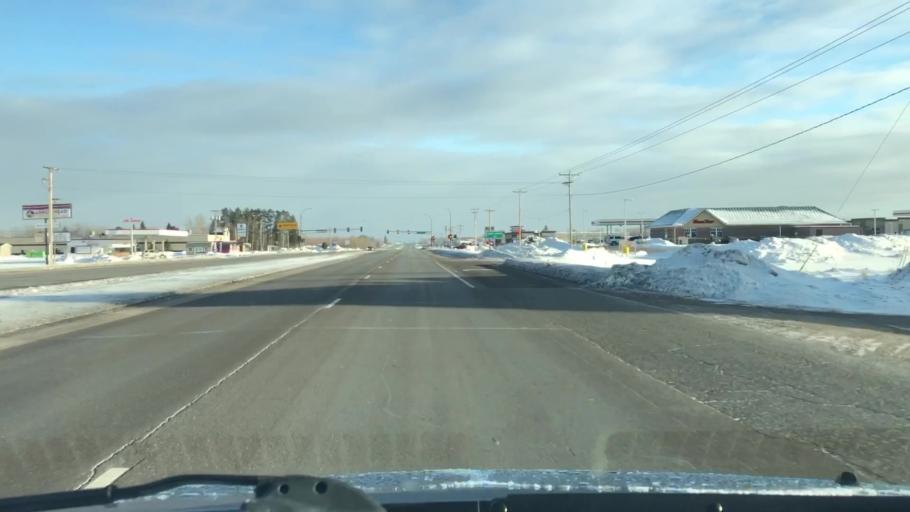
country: US
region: Minnesota
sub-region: Saint Louis County
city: Hermantown
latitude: 46.8351
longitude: -92.2080
